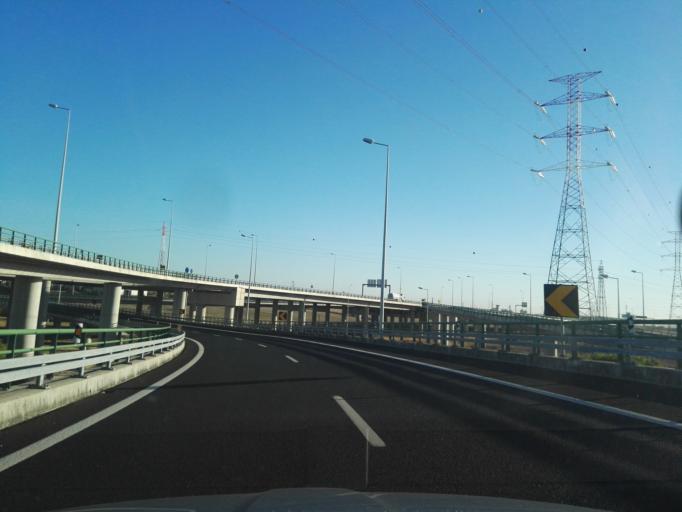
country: PT
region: Lisbon
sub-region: Alenquer
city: Carregado
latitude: 39.0160
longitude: -8.9653
